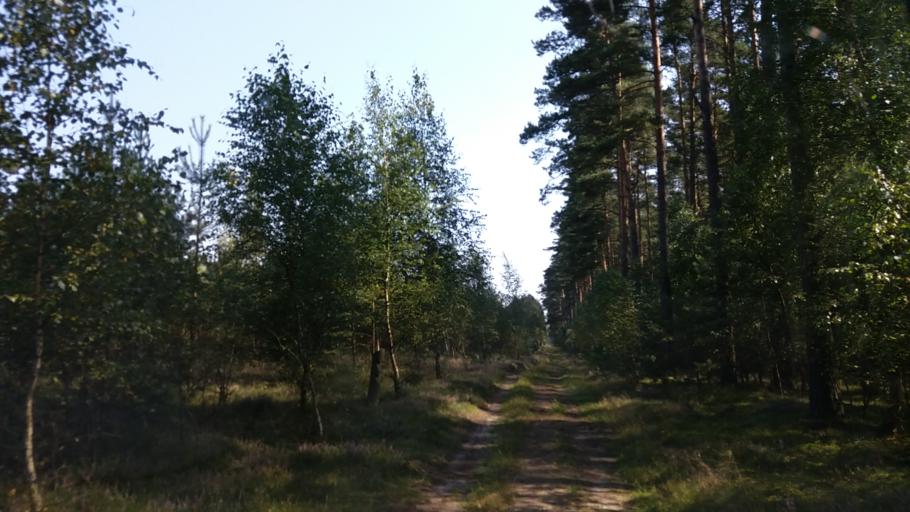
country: PL
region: West Pomeranian Voivodeship
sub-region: Powiat drawski
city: Kalisz Pomorski
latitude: 53.1299
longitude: 15.9401
